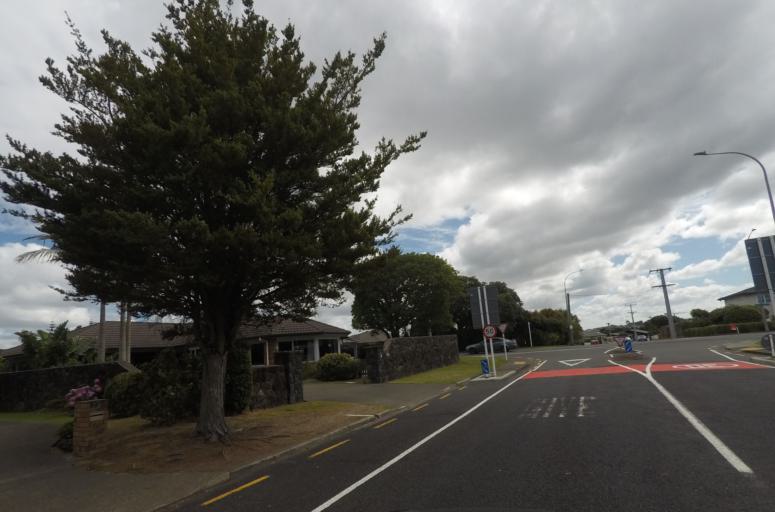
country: NZ
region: Auckland
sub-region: Auckland
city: Rothesay Bay
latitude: -36.5891
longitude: 174.6936
